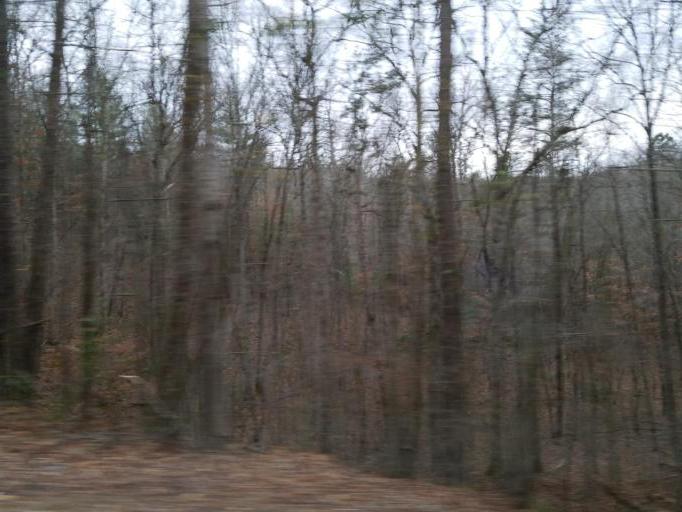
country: US
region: Georgia
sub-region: Dawson County
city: Dawsonville
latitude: 34.4081
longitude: -84.0186
